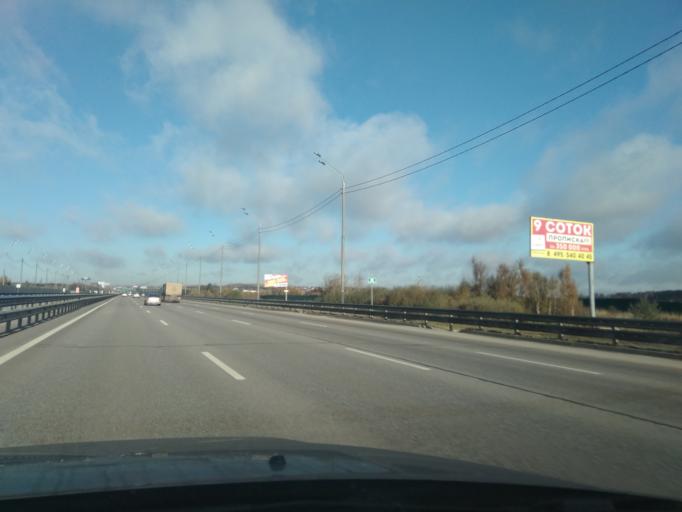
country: RU
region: Moskovskaya
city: Pavlovskaya Sloboda
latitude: 55.7928
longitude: 37.0533
